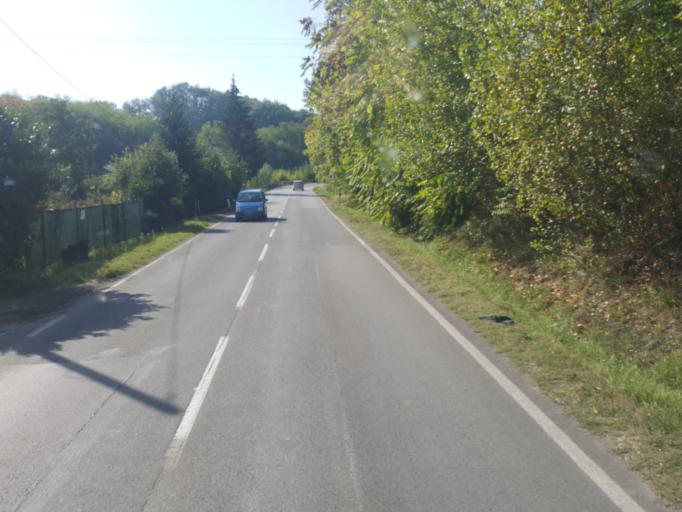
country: IT
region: Tuscany
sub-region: Provincia di Siena
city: Colle di Val d'Elsa
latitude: 43.4132
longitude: 11.1194
